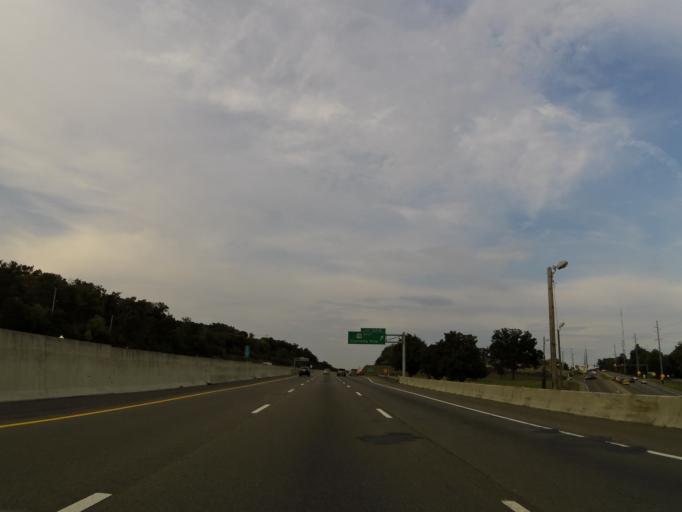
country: US
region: Tennessee
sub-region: Davidson County
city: Belle Meade
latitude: 36.1309
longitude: -86.8983
